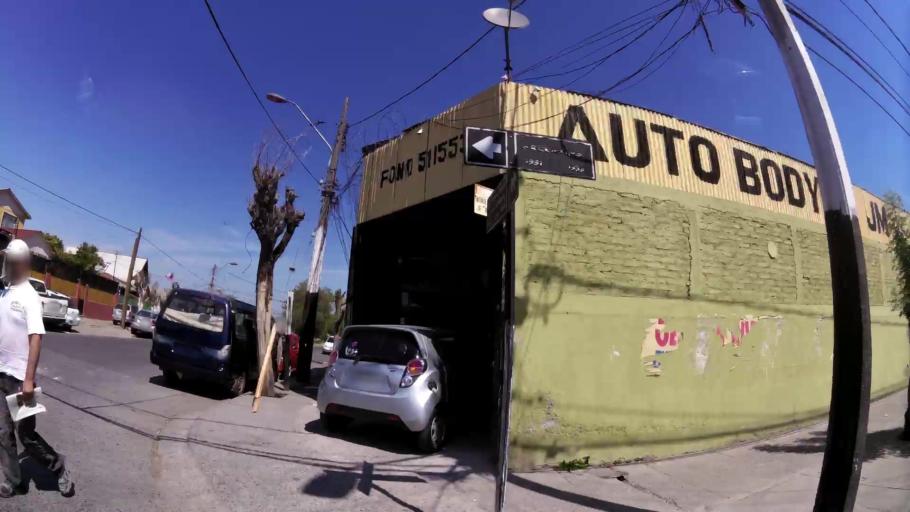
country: CL
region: Santiago Metropolitan
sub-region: Provincia de Santiago
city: La Pintana
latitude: -33.5327
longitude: -70.6371
